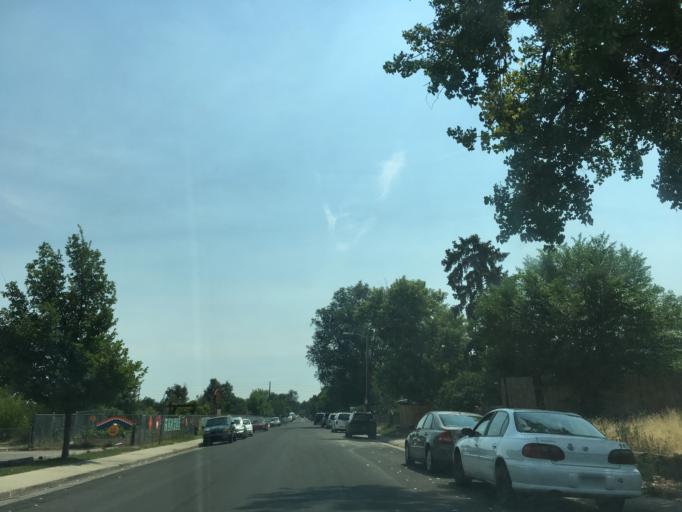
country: US
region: Colorado
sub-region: Jefferson County
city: Lakewood
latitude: 39.7067
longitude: -105.0321
